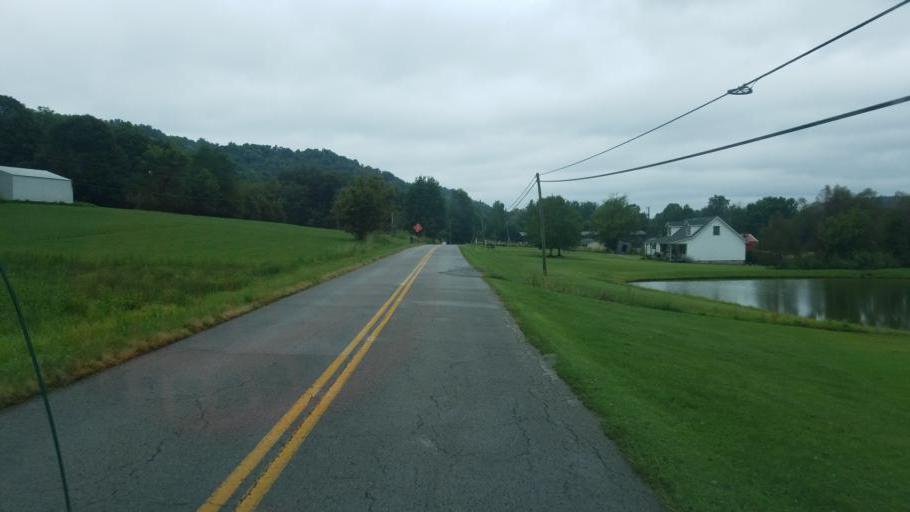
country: US
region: Kentucky
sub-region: Rowan County
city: Morehead
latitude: 38.3389
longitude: -83.5366
